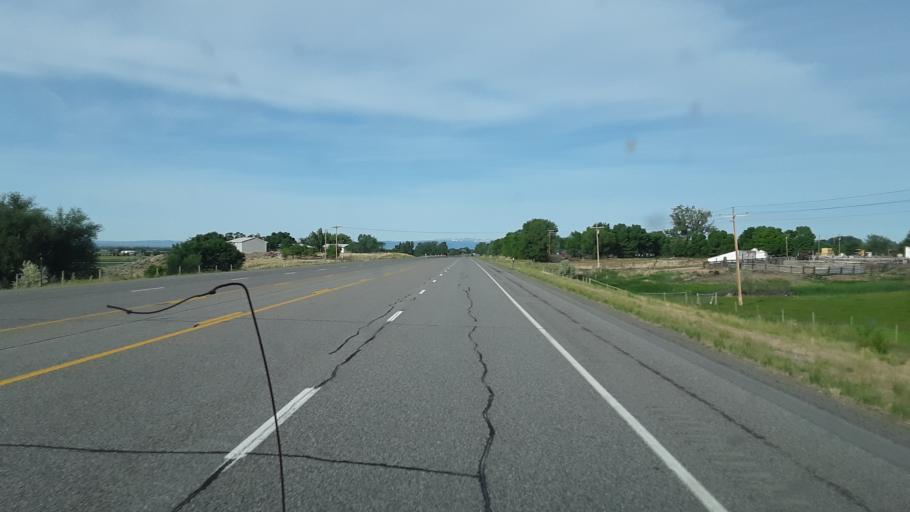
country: US
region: Wyoming
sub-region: Fremont County
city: Riverton
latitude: 43.1008
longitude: -108.3542
